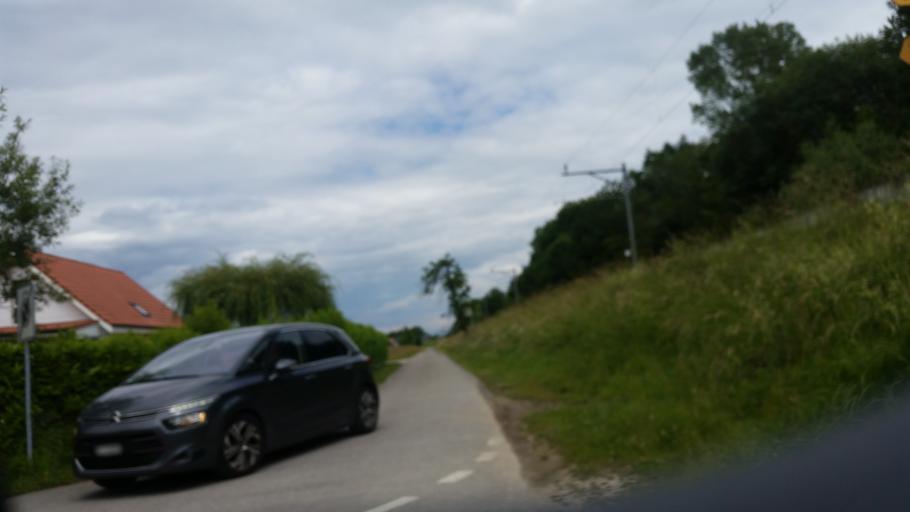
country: CH
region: Vaud
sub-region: Jura-Nord vaudois District
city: Yvonand
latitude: 46.8068
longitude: 6.7703
